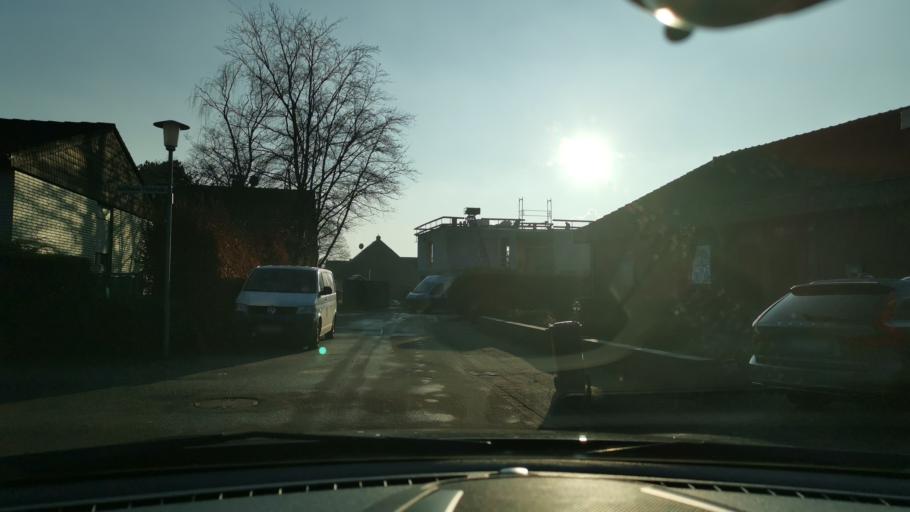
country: DE
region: North Rhine-Westphalia
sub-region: Regierungsbezirk Dusseldorf
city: Neuss
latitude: 51.1462
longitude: 6.7160
